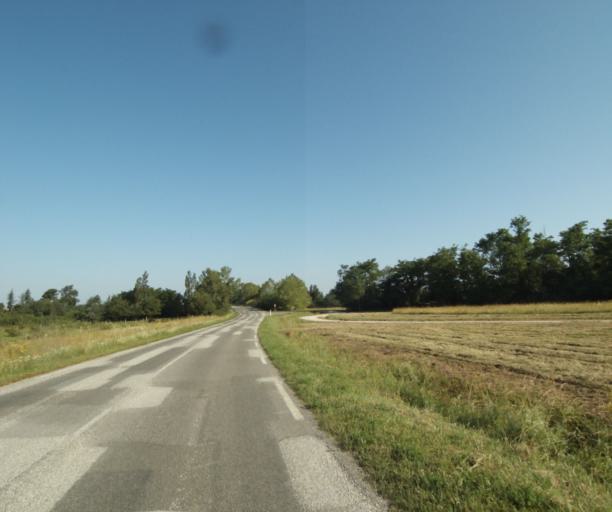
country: FR
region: Midi-Pyrenees
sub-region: Departement du Tarn-et-Garonne
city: Montauban
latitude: 44.0159
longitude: 1.3899
